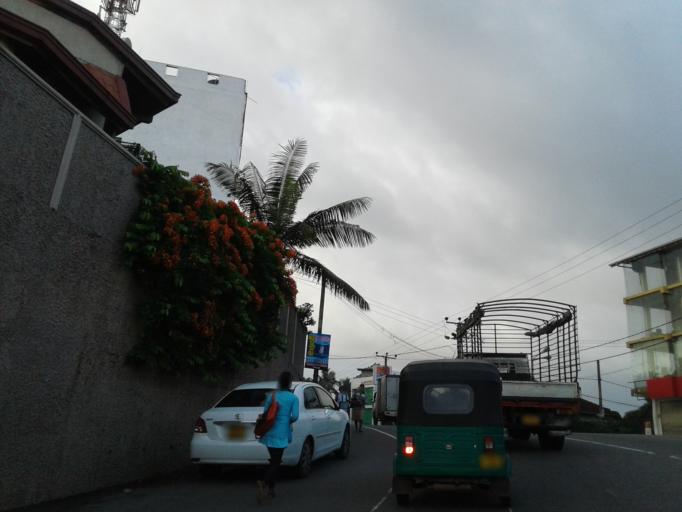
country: LK
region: Western
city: Mulleriyawa
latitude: 6.9340
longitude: 79.9824
